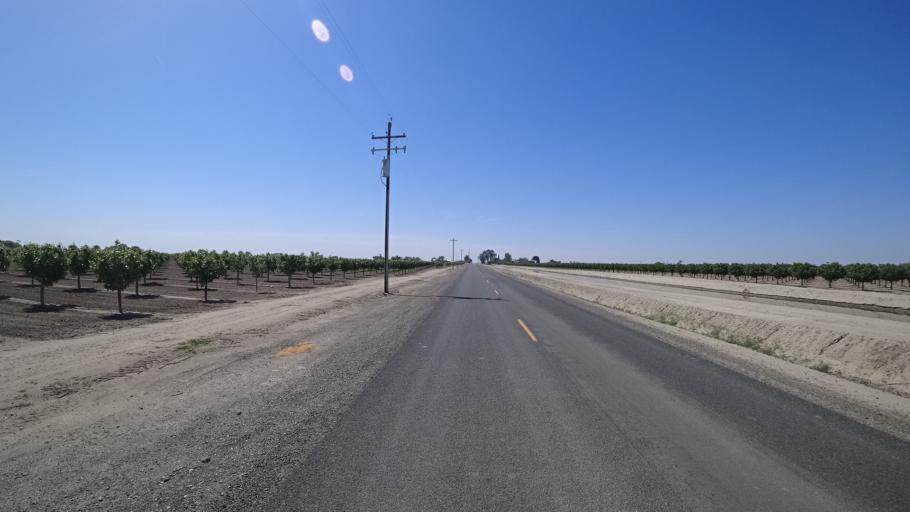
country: US
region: California
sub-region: Kings County
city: Corcoran
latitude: 36.0411
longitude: -119.5361
